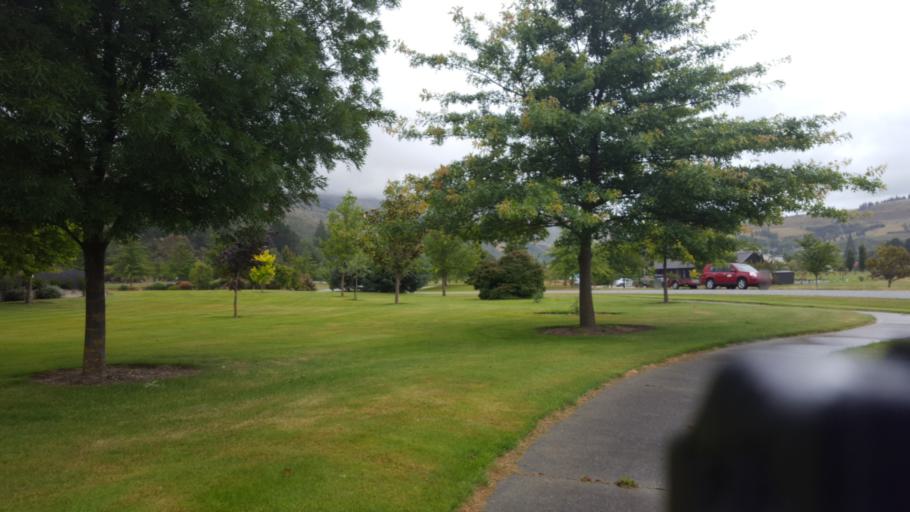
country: NZ
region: Otago
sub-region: Queenstown-Lakes District
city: Wanaka
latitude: -45.1972
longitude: 169.3180
